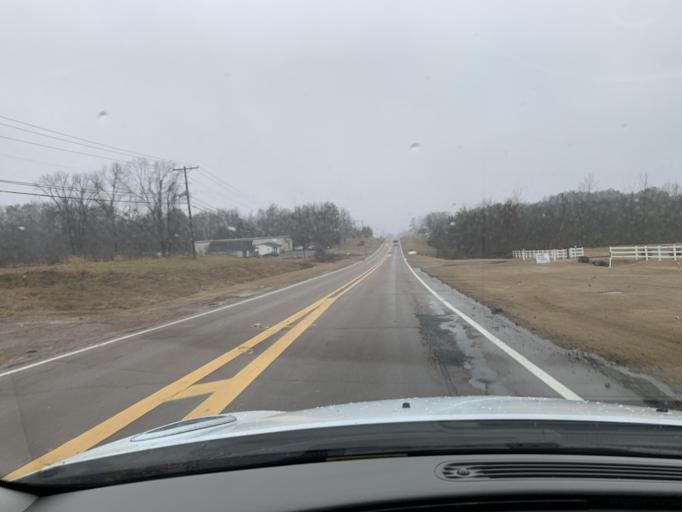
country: US
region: Mississippi
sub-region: De Soto County
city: Horn Lake
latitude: 34.9011
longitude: -89.9972
